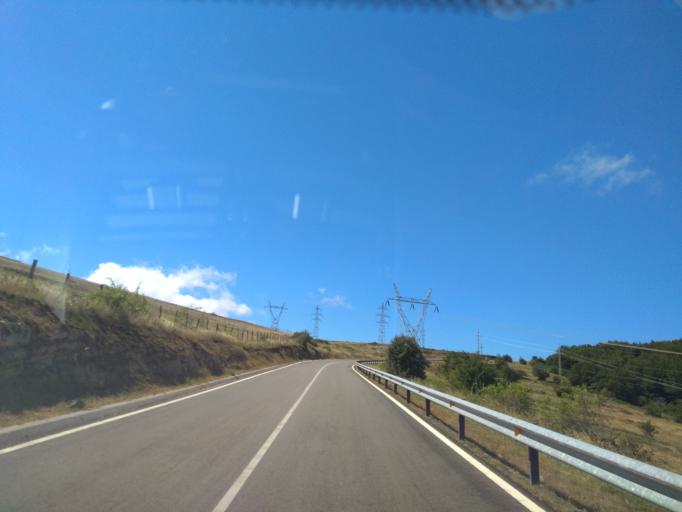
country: ES
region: Cantabria
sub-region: Provincia de Cantabria
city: Villaescusa
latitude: 42.9448
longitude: -4.1505
